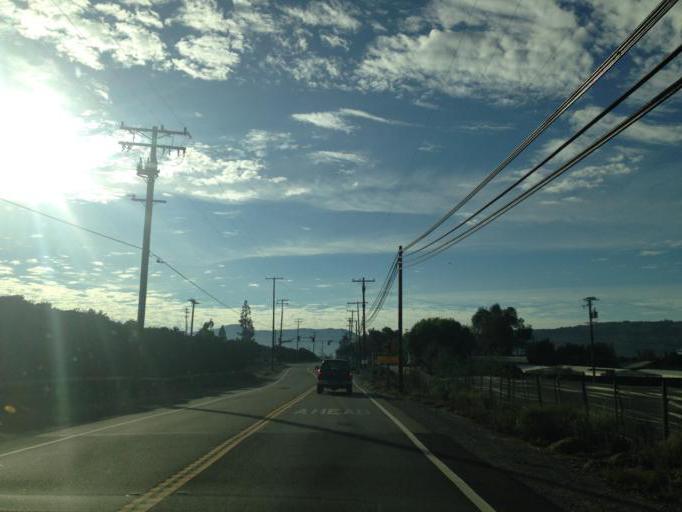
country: US
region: California
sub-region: San Diego County
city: Valley Center
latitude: 33.3312
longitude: -117.0020
